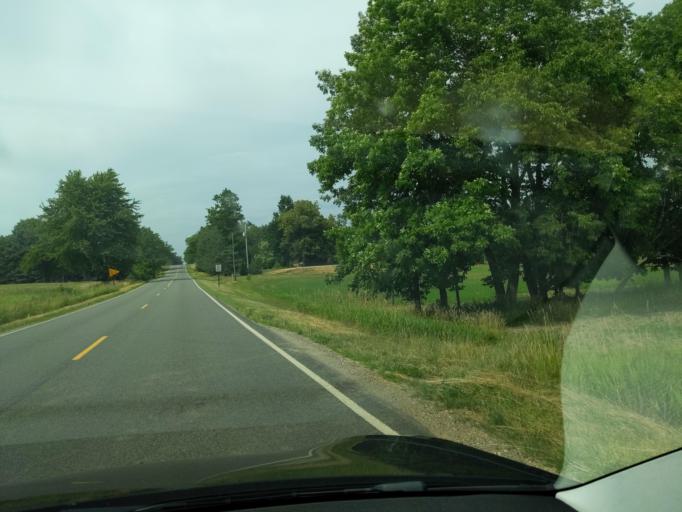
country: US
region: Michigan
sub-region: Clinton County
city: DeWitt
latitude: 42.8820
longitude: -84.6023
